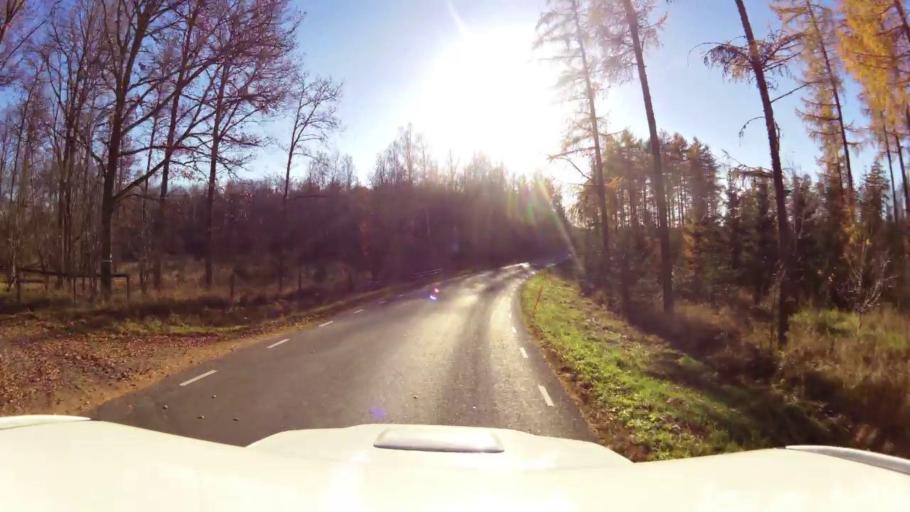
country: SE
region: OEstergoetland
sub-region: Linkopings Kommun
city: Sturefors
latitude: 58.2564
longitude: 15.6634
